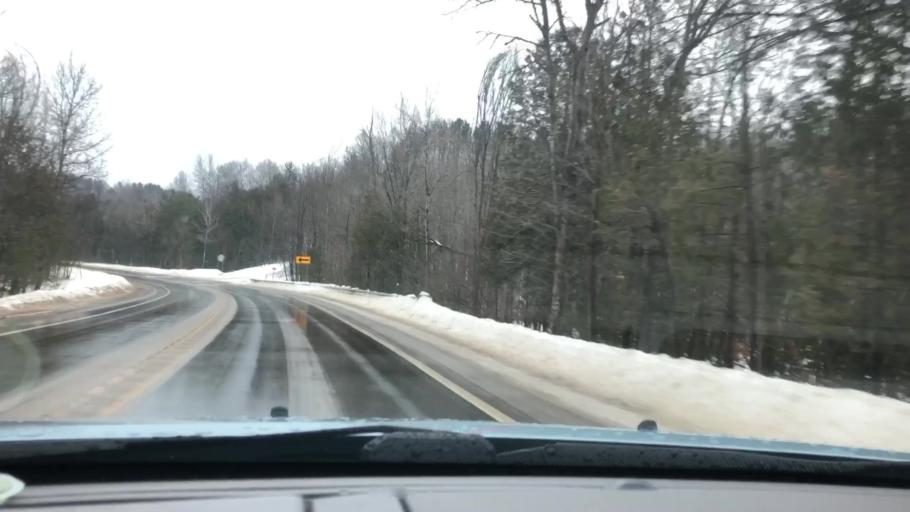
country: US
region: Michigan
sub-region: Charlevoix County
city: East Jordan
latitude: 45.1304
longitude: -85.0809
